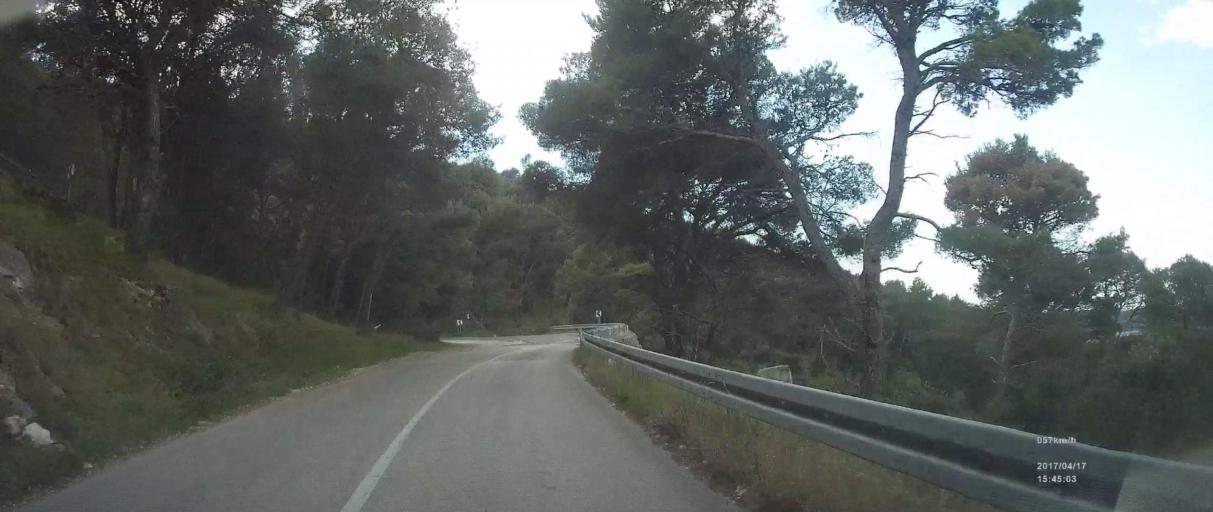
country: HR
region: Sibensko-Kniniska
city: Primosten
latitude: 43.6276
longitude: 15.9615
